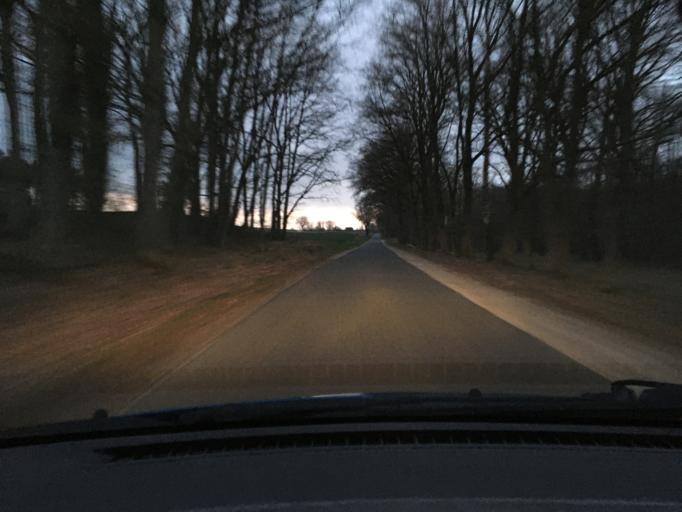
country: DE
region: Lower Saxony
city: Neetze
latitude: 53.2337
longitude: 10.6325
